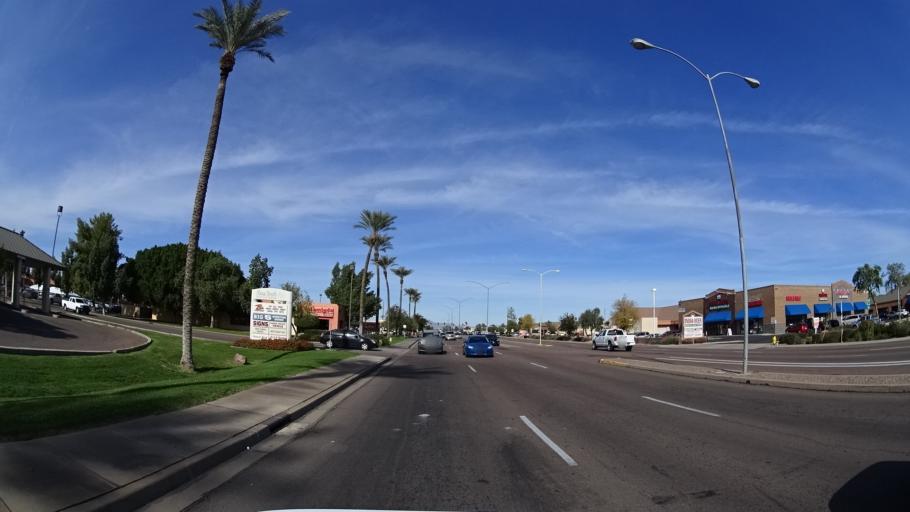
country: US
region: Arizona
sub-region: Maricopa County
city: Gilbert
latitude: 33.3912
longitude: -111.7884
